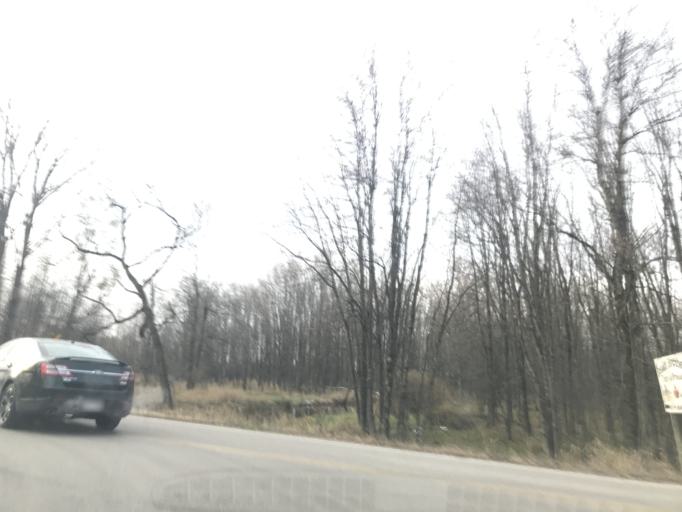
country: US
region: Wisconsin
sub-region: Marinette County
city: Peshtigo
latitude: 45.0620
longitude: -87.7999
